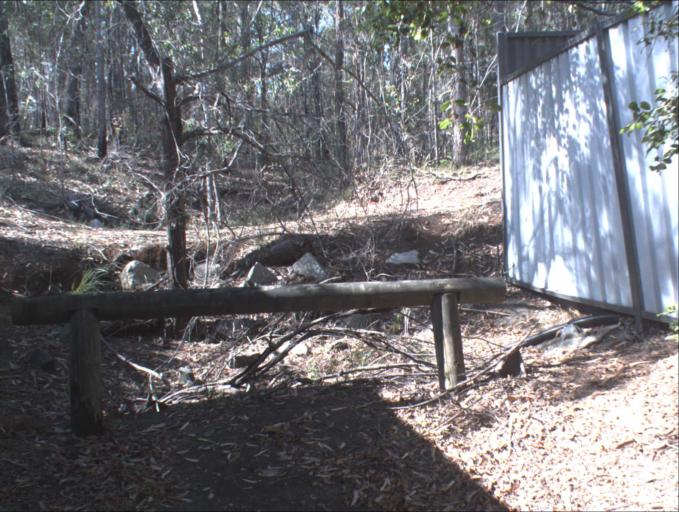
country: AU
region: Queensland
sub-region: Logan
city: Slacks Creek
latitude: -27.6409
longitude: 153.1882
